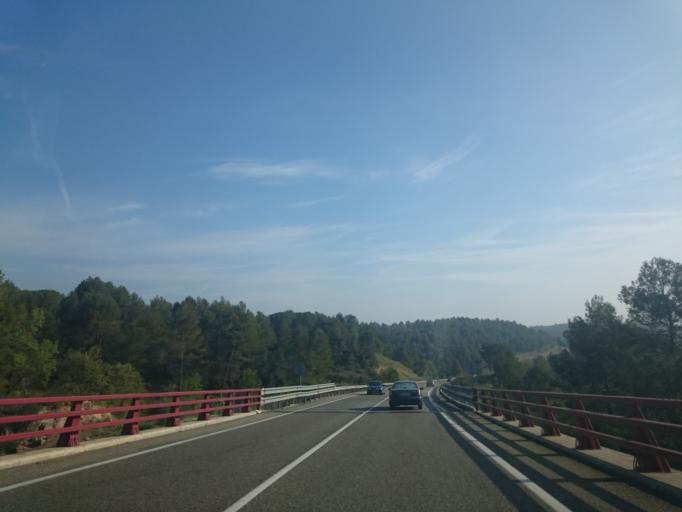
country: ES
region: Catalonia
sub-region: Provincia de Barcelona
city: Sant Salvador de Guardiola
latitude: 41.6843
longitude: 1.7552
